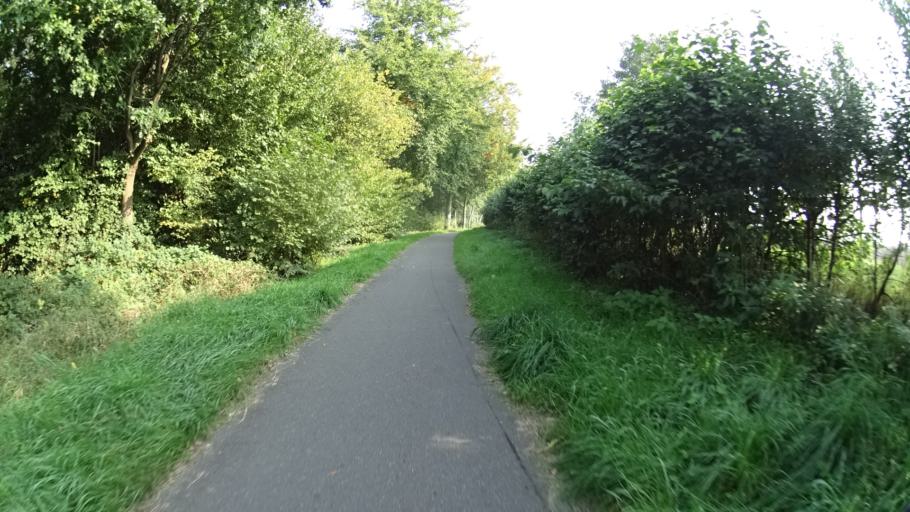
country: DE
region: Lower Saxony
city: Reppenstedt
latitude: 53.2188
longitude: 10.3505
